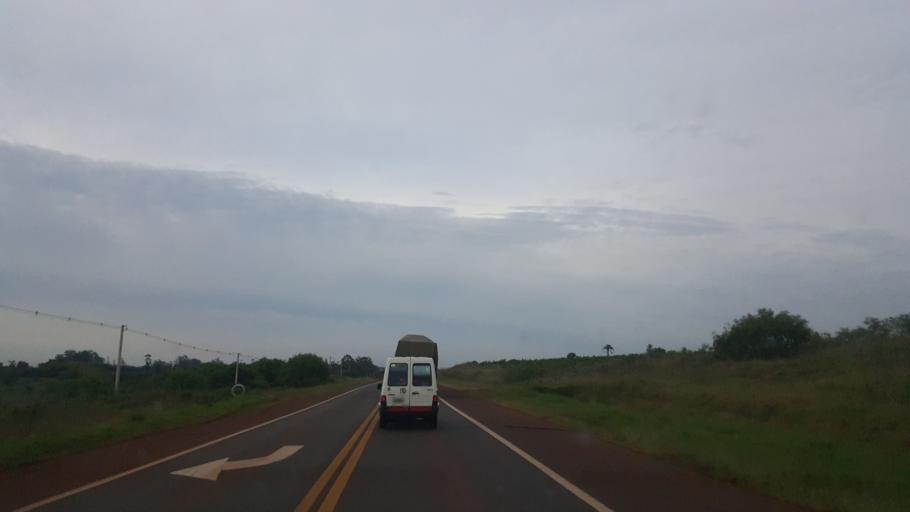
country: AR
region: Misiones
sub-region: Departamento de Apostoles
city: San Jose
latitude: -27.7676
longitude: -55.8026
